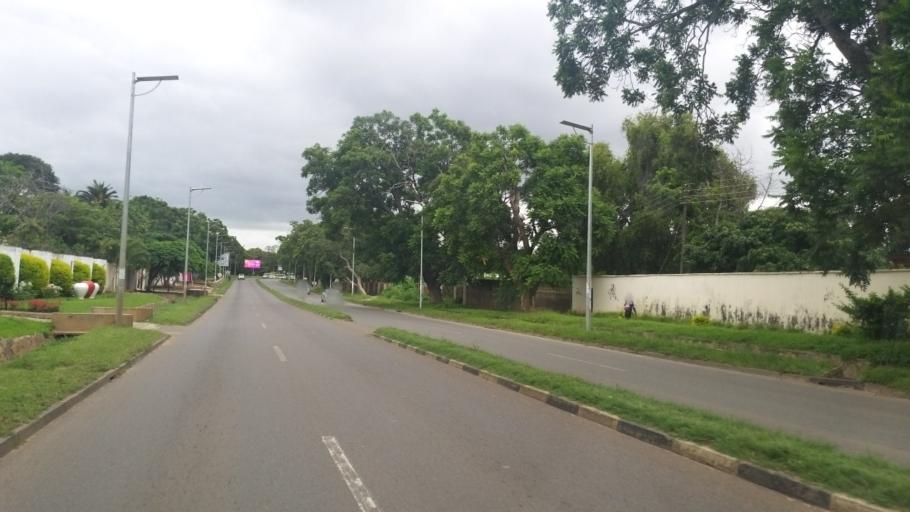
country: ZM
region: Lusaka
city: Lusaka
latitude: -15.4200
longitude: 28.3175
